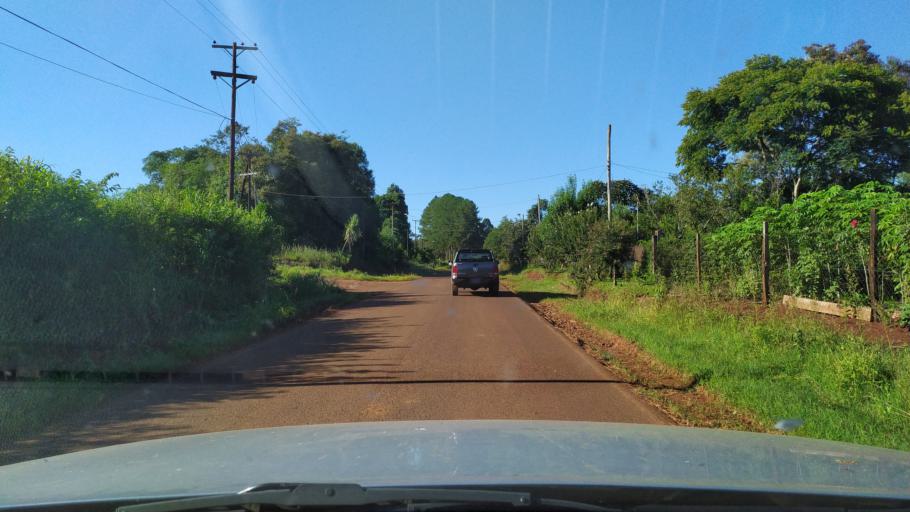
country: AR
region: Misiones
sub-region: Departamento de Montecarlo
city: Montecarlo
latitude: -26.6016
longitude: -54.7021
